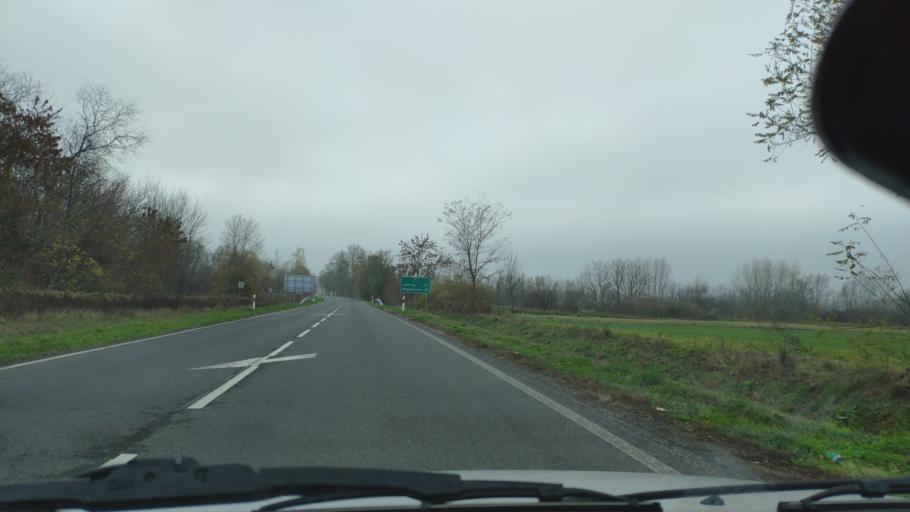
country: HU
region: Somogy
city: Balatonbereny
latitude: 46.6410
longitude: 17.2990
